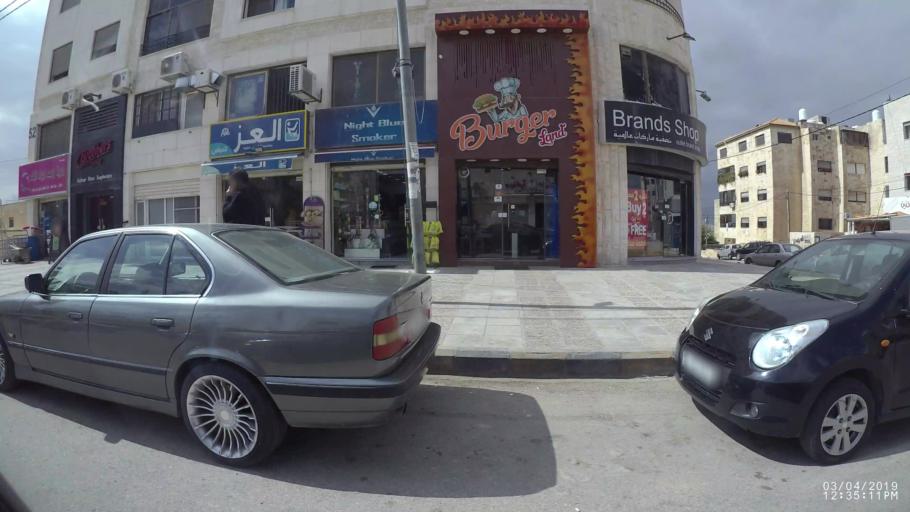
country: JO
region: Amman
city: Wadi as Sir
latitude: 31.9588
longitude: 35.8371
